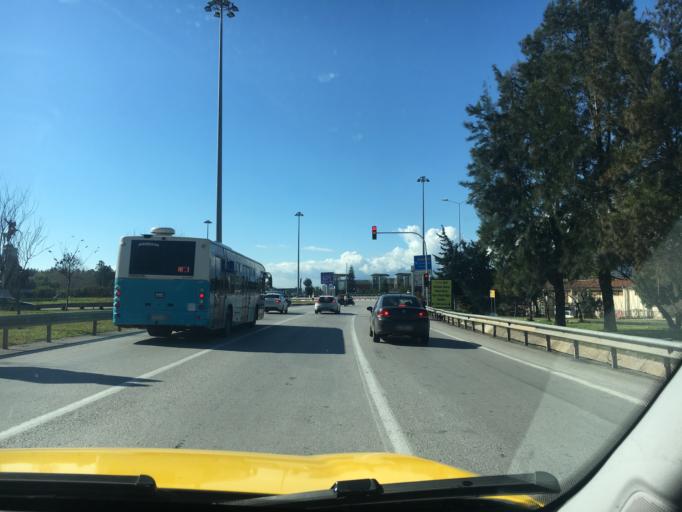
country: TR
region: Antalya
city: Antalya
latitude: 36.8862
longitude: 30.6629
